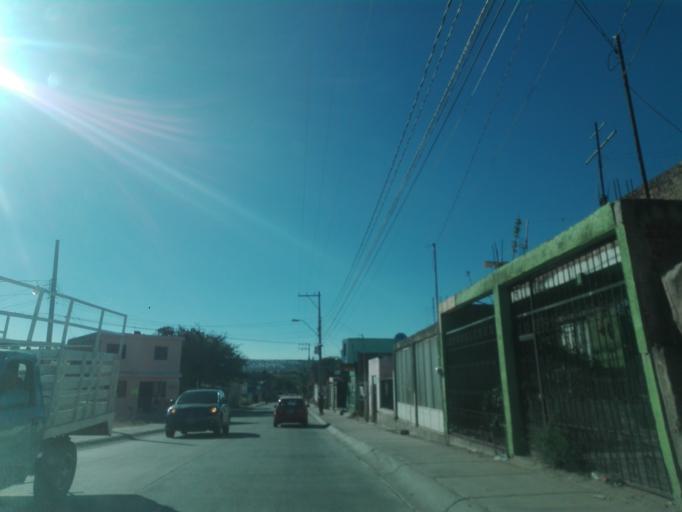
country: MX
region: Guanajuato
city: Leon
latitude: 21.1880
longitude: -101.6774
